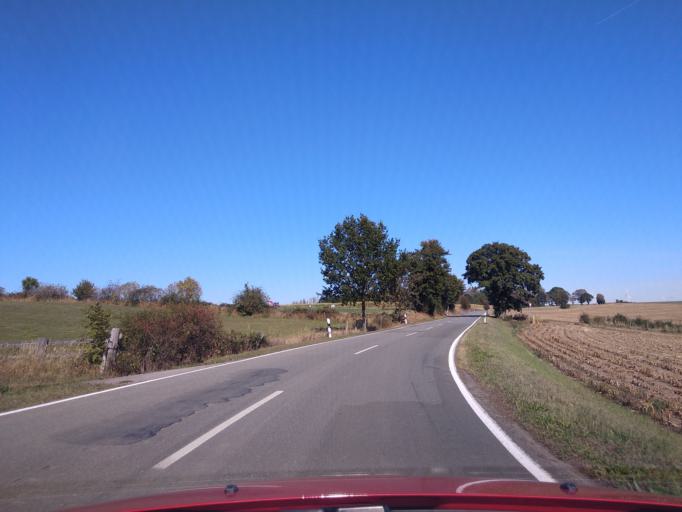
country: DE
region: Lower Saxony
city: Boffzen
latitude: 51.7396
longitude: 9.2981
